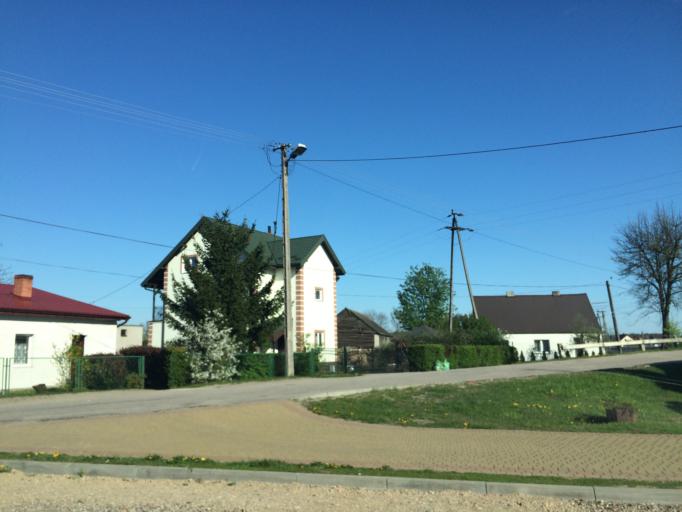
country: PL
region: Warmian-Masurian Voivodeship
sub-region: Powiat dzialdowski
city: Rybno
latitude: 53.3991
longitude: 19.8423
